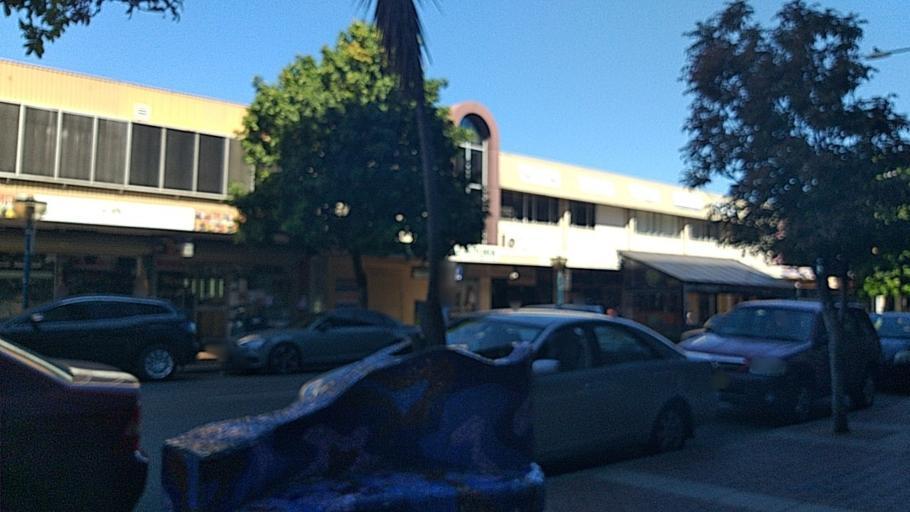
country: AU
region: New South Wales
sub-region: Fairfield
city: Liverpool
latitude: -33.9229
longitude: 150.9224
